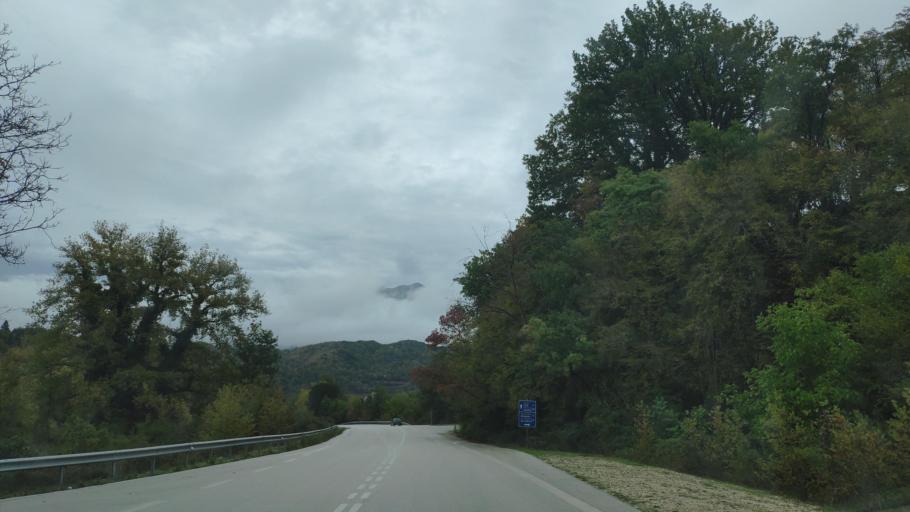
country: GR
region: Epirus
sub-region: Nomos Thesprotias
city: Paramythia
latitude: 39.5037
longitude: 20.6807
